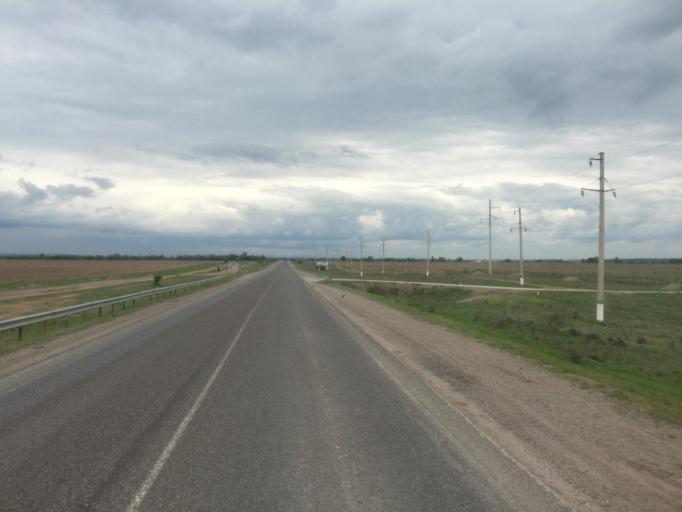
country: KG
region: Chuy
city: Sokuluk
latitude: 43.2461
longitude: 74.3021
